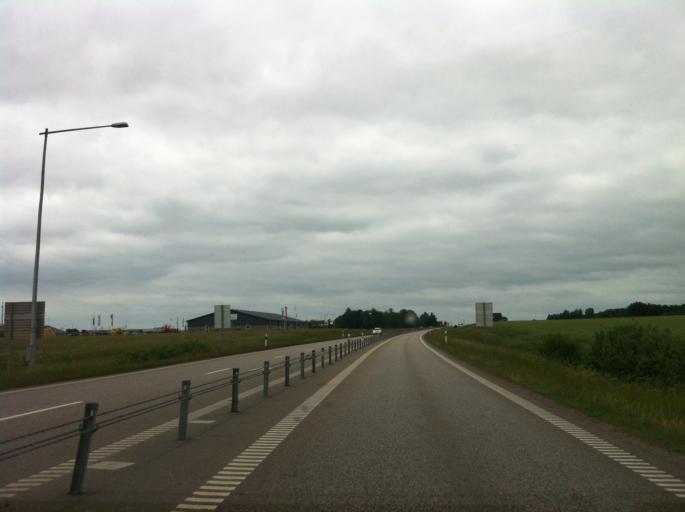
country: SE
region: Skane
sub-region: Eslovs Kommun
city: Eslov
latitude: 55.7993
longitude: 13.3870
